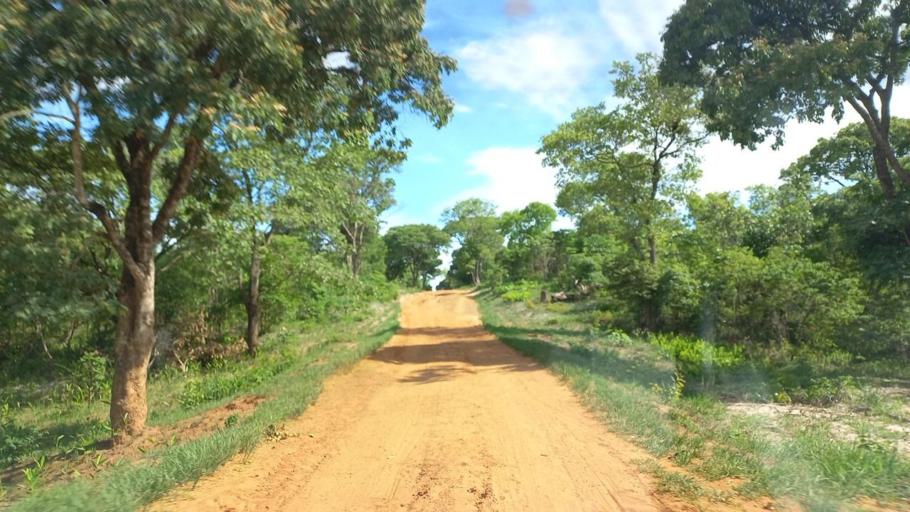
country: ZM
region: North-Western
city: Kabompo
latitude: -13.0701
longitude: 24.2182
